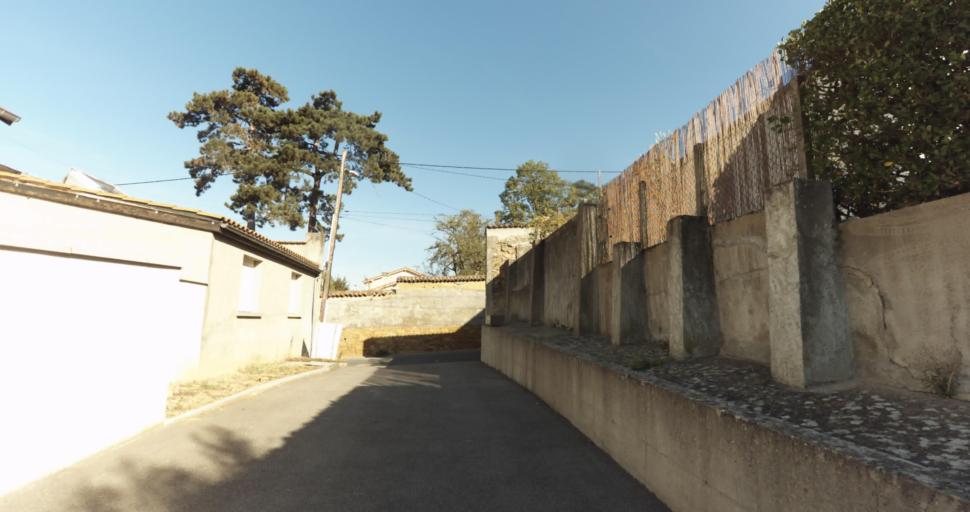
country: FR
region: Rhone-Alpes
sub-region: Departement du Rhone
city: Neuville-sur-Saone
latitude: 45.8834
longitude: 4.8382
